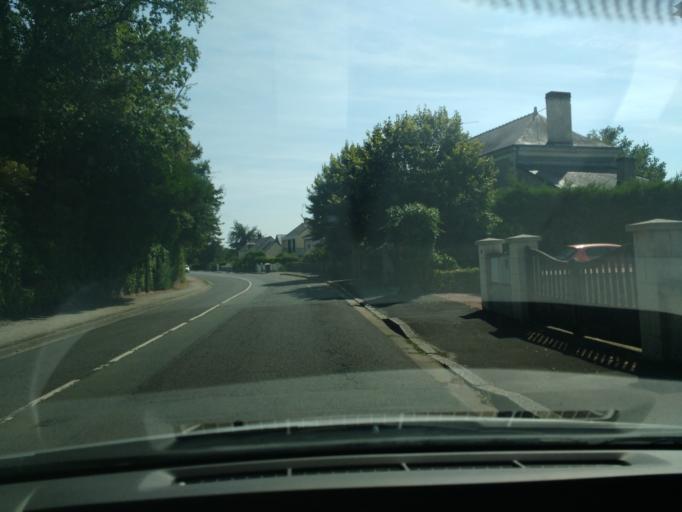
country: FR
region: Pays de la Loire
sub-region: Departement de Maine-et-Loire
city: Trelaze
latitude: 47.4667
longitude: -0.4898
